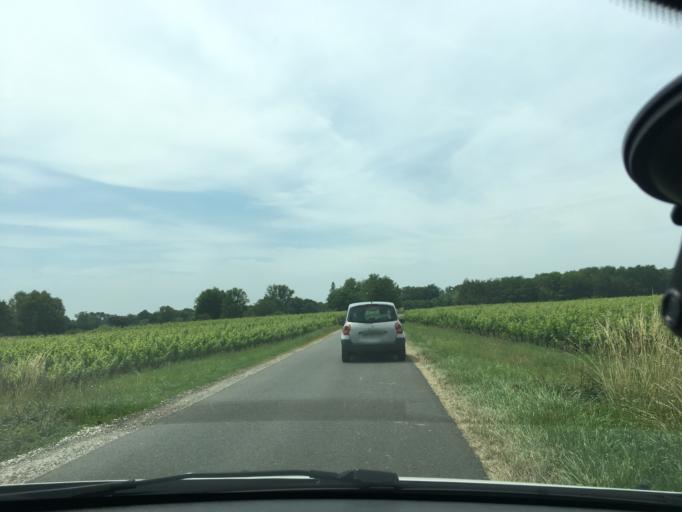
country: FR
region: Aquitaine
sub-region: Departement de la Gironde
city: Listrac-Medoc
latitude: 45.0550
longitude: -0.8073
